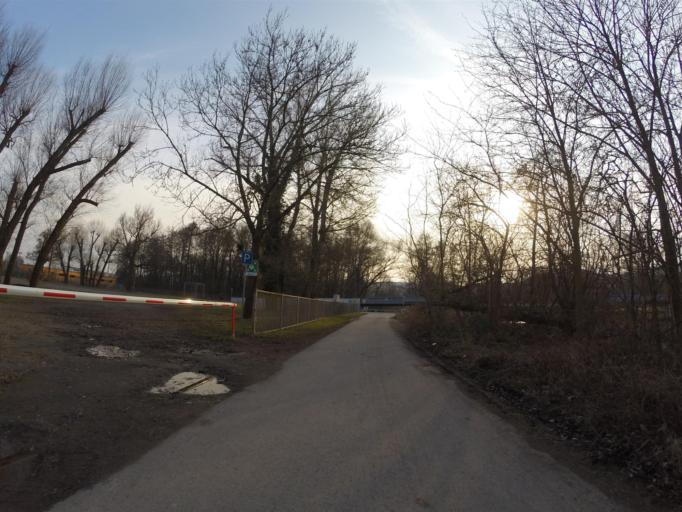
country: DE
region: Thuringia
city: Jena
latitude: 50.9155
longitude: 11.5815
